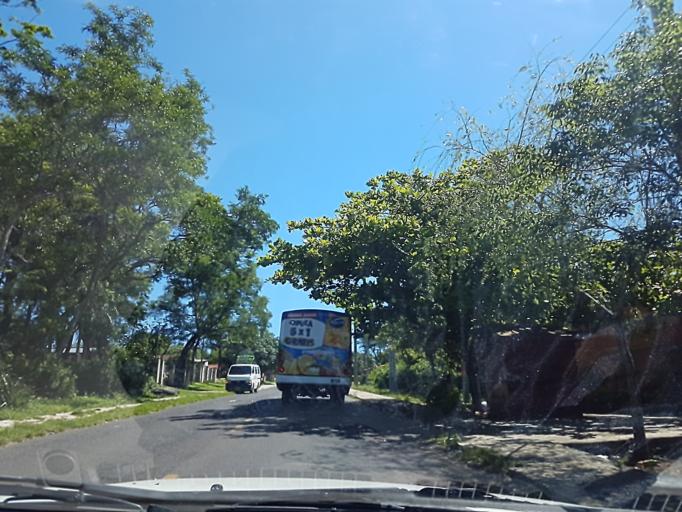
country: PY
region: Cordillera
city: Altos
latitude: -25.2591
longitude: -57.2475
